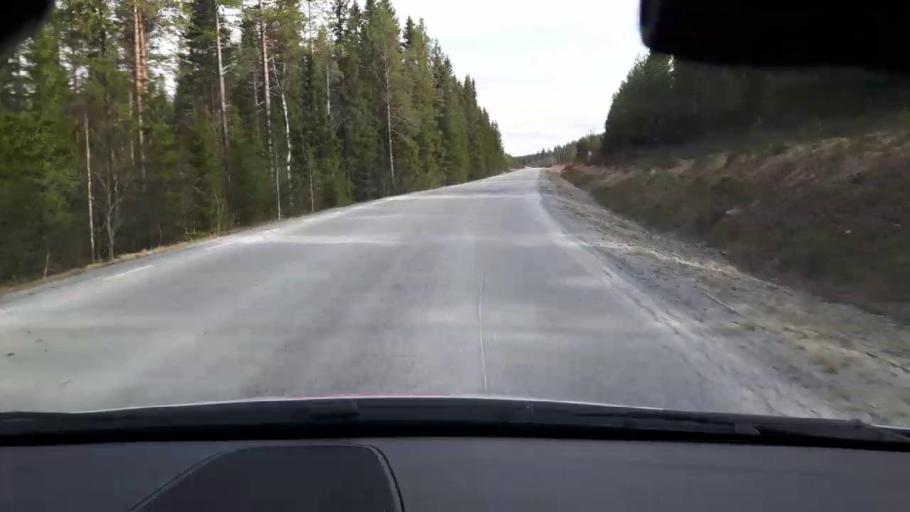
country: SE
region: Jaemtland
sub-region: Bergs Kommun
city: Hoverberg
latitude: 62.7181
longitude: 14.6060
